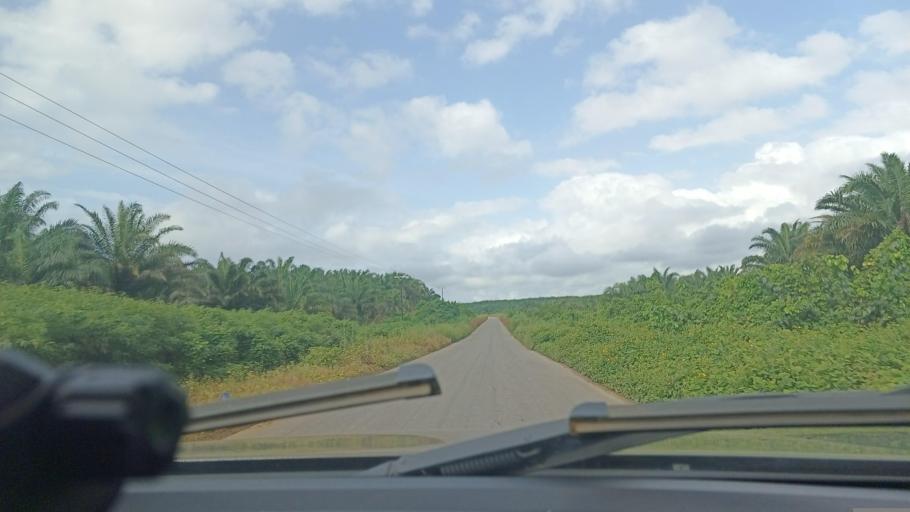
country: LR
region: Bomi
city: Tubmanburg
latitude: 6.7271
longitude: -11.0393
